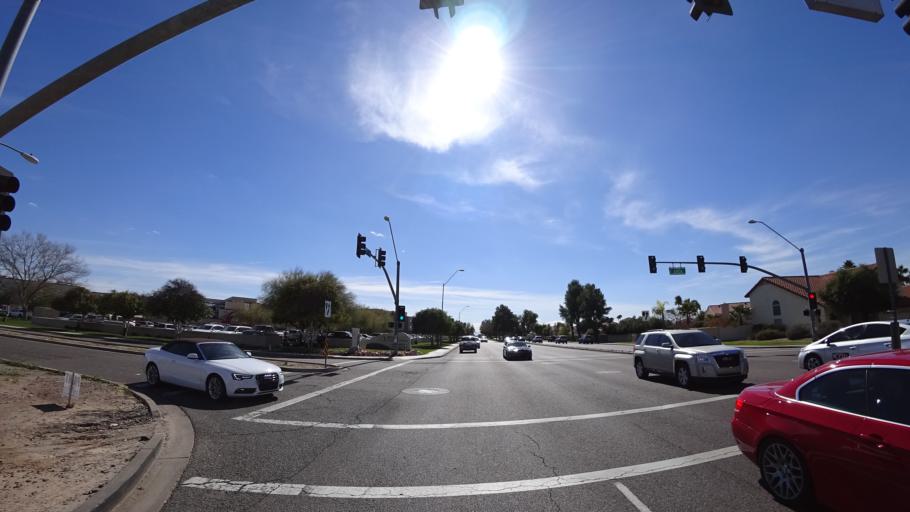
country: US
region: Arizona
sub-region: Maricopa County
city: Peoria
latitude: 33.6565
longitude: -112.2029
